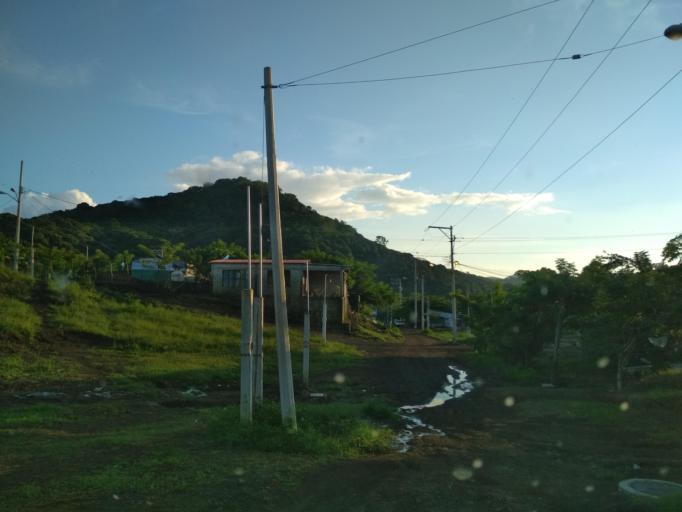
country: MX
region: Veracruz
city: Catemaco
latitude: 18.4222
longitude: -95.1237
